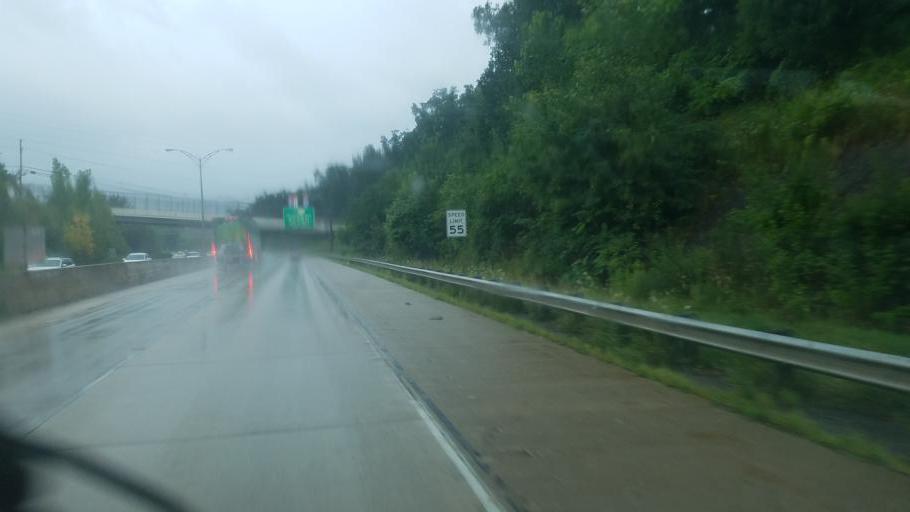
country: US
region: Ohio
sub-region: Trumbull County
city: Churchill
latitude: 41.1426
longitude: -80.6791
